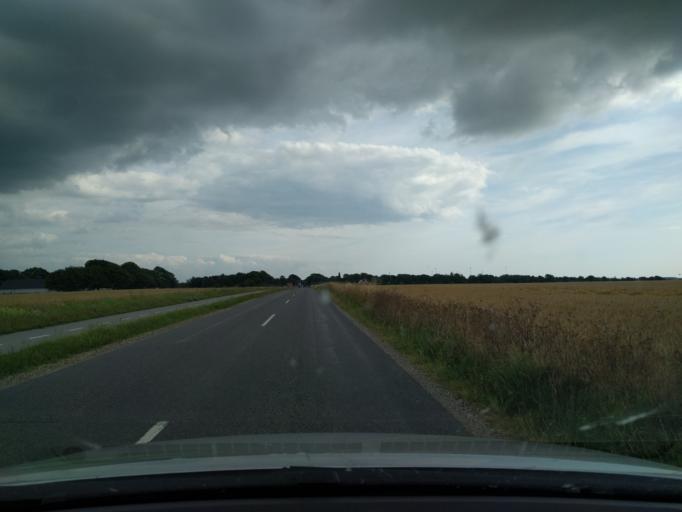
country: DK
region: Central Jutland
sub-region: Herning Kommune
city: Snejbjerg
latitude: 56.0980
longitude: 8.9102
